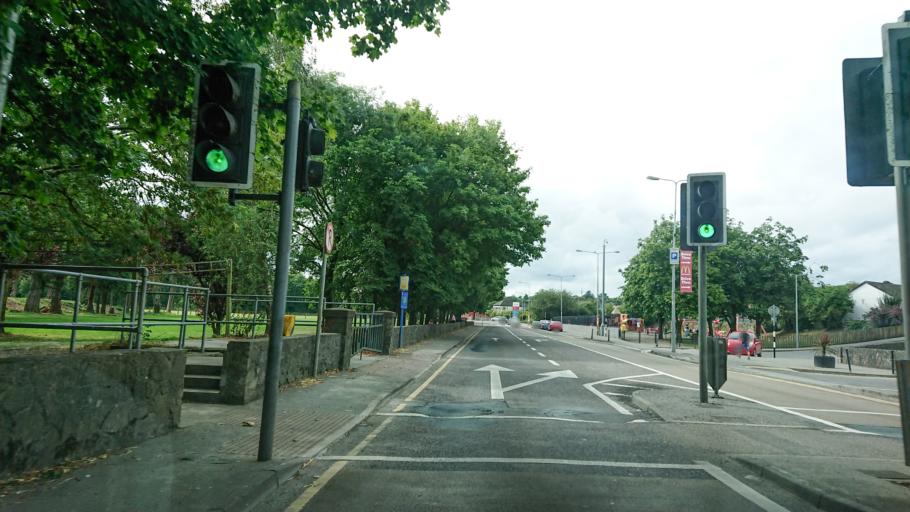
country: IE
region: Munster
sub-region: County Cork
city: Mallow
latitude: 52.1353
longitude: -8.6446
